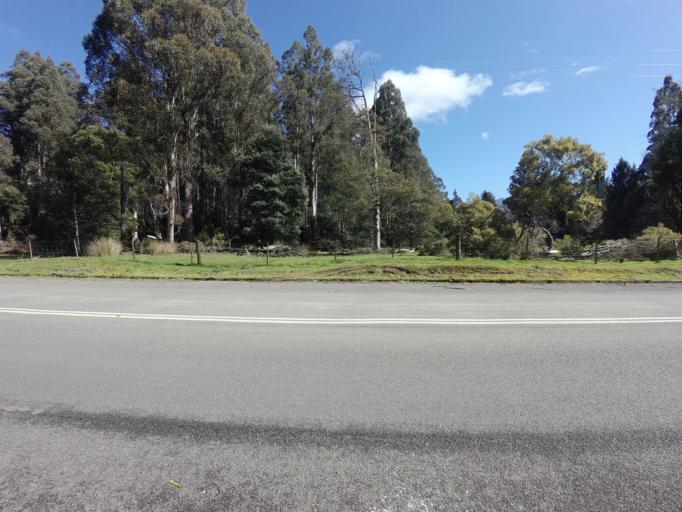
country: AU
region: Tasmania
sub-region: Derwent Valley
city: New Norfolk
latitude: -42.7642
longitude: 146.6000
